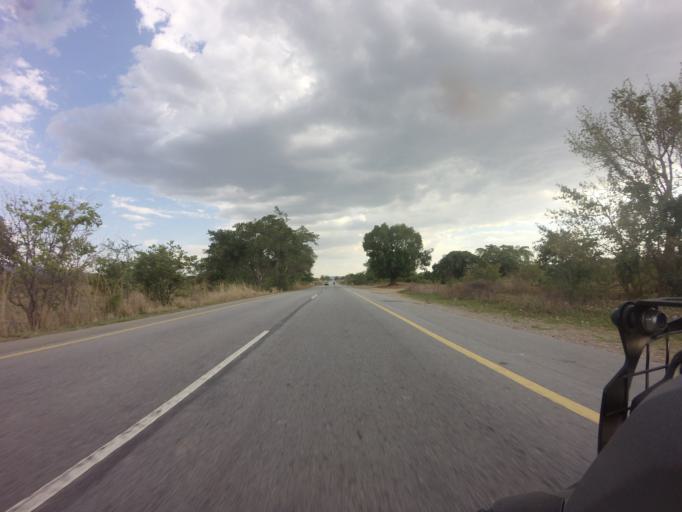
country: AO
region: Huila
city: Lubango
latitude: -14.3724
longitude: 14.0403
